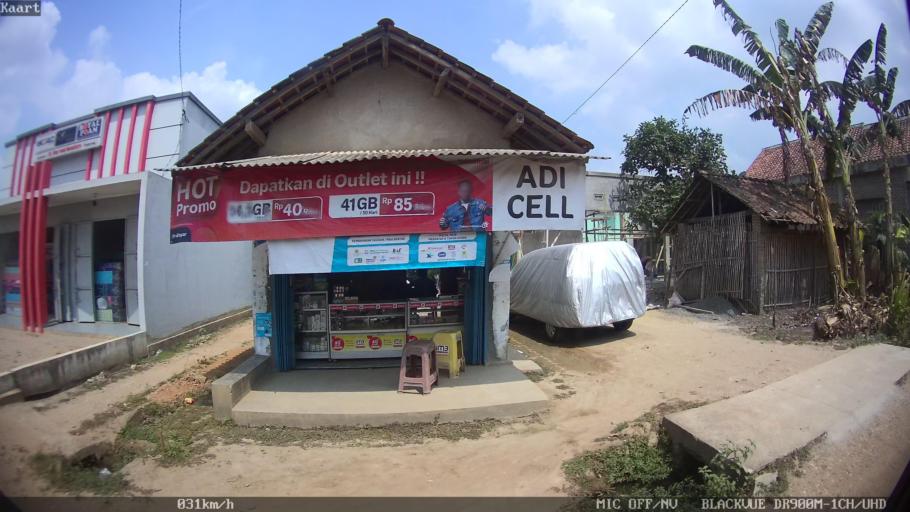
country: ID
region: Lampung
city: Pringsewu
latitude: -5.3861
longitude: 104.9696
